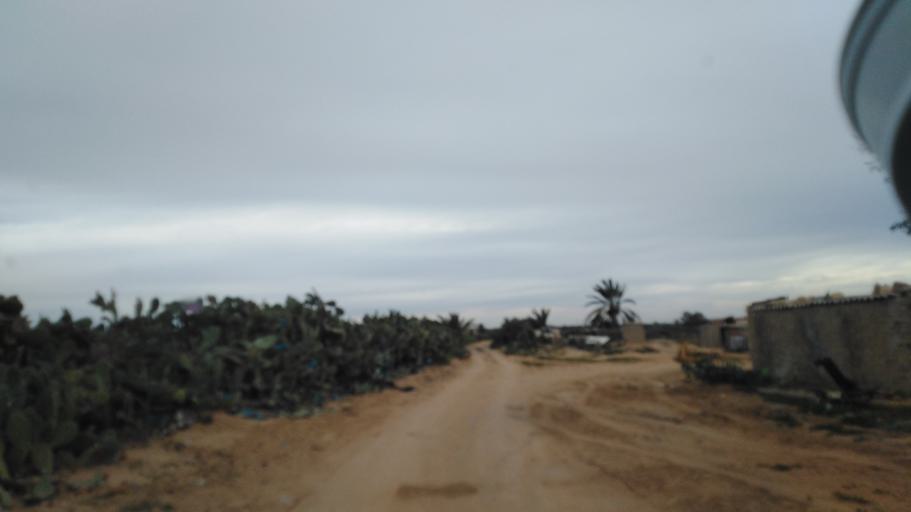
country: TN
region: Safaqis
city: Bi'r `Ali Bin Khalifah
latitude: 34.7651
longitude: 10.3769
